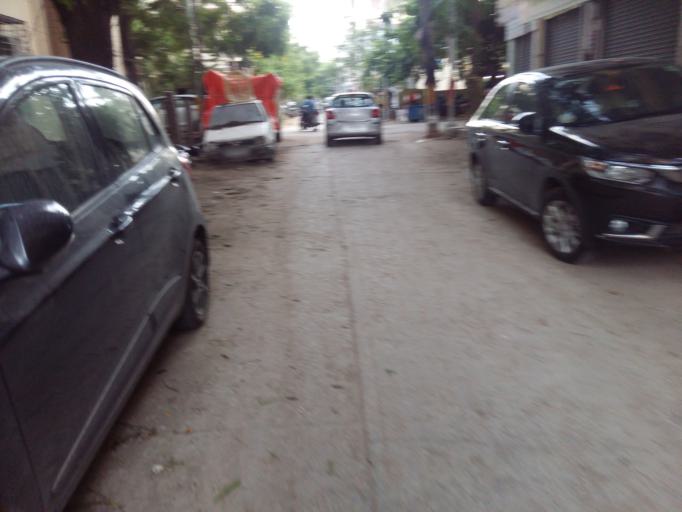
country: IN
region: Telangana
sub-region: Rangareddi
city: Kukatpalli
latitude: 17.4884
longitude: 78.3979
